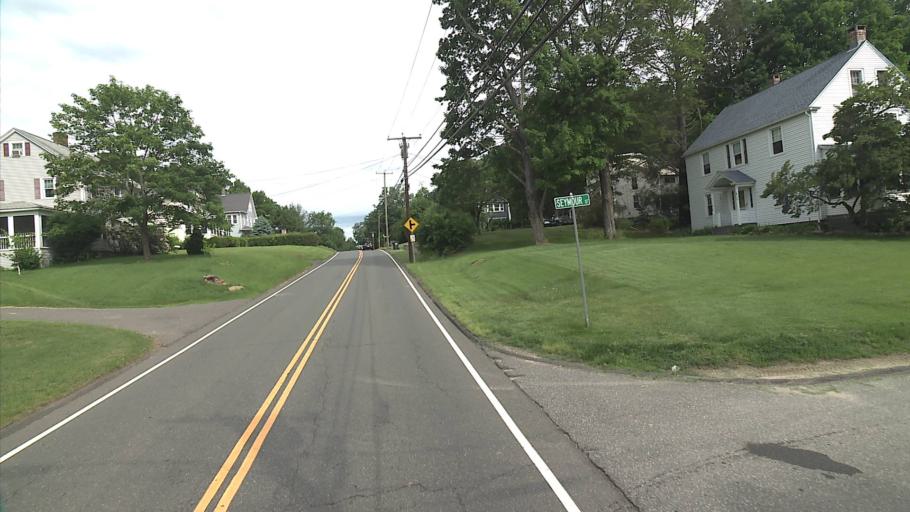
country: US
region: Connecticut
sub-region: Litchfield County
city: Watertown
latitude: 41.6106
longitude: -73.1224
